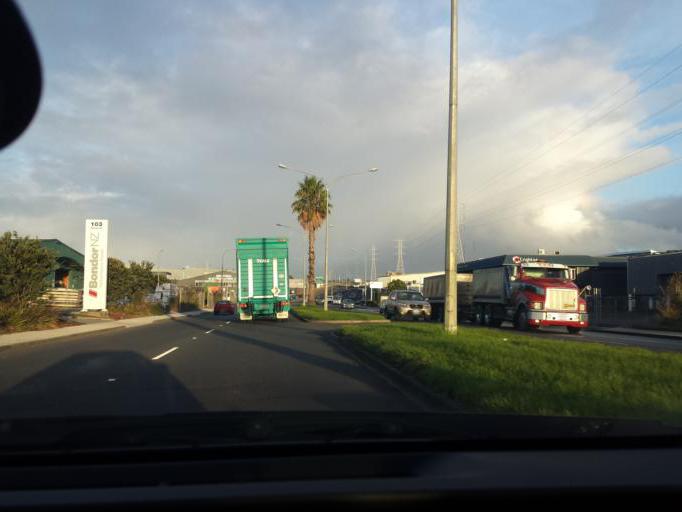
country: NZ
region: Auckland
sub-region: Auckland
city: Mangere
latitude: -36.9266
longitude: 174.7897
